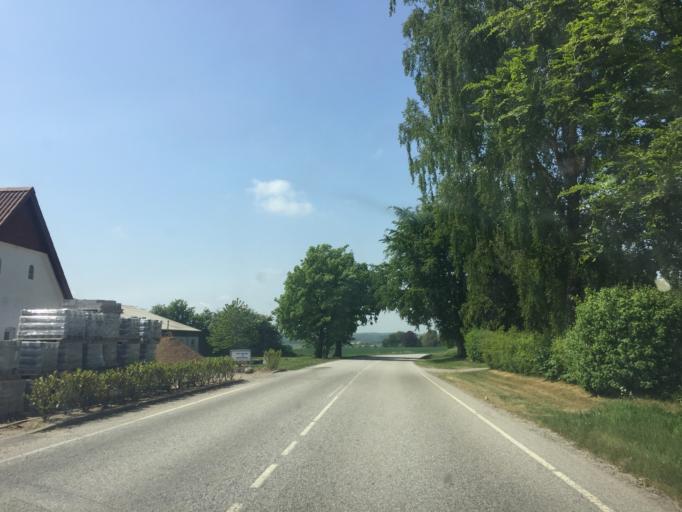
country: DK
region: South Denmark
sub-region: Kolding Kommune
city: Sonder Bjert
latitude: 55.3731
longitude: 9.5936
